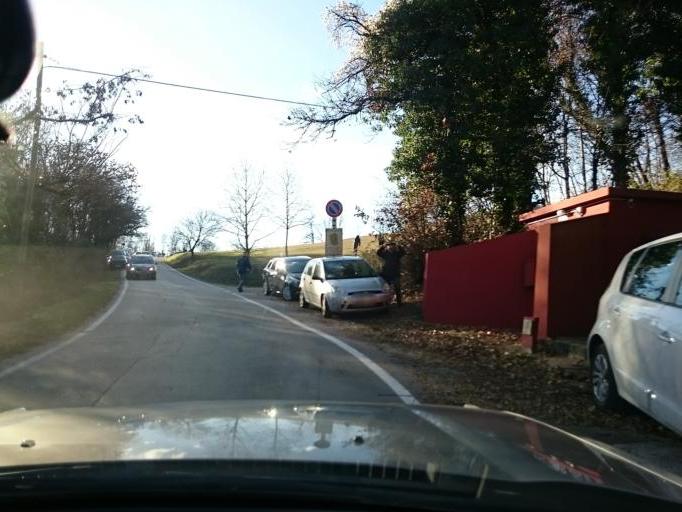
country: IT
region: Veneto
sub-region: Provincia di Padova
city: Bastia
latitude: 45.3575
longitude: 11.6676
